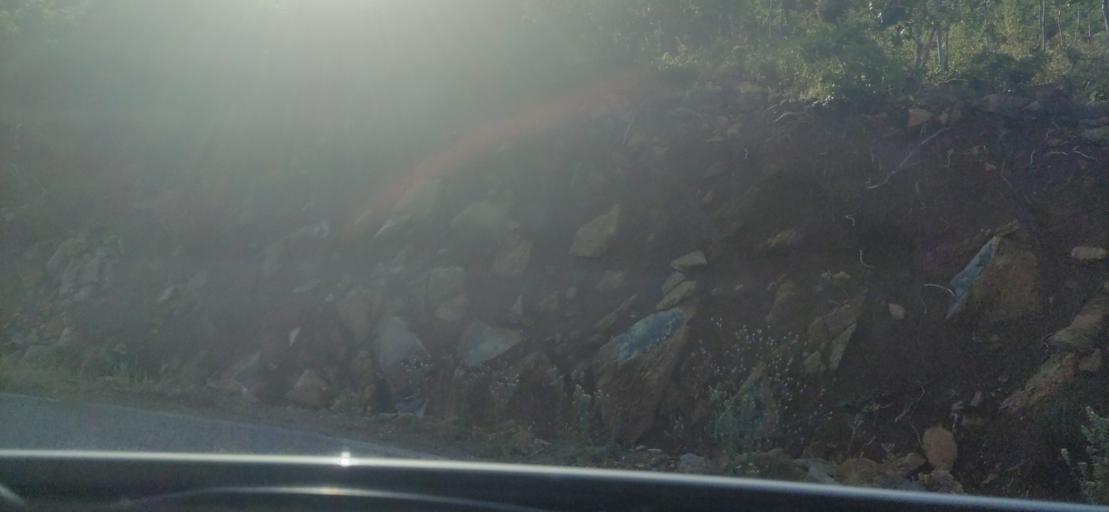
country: AL
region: Shkoder
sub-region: Rrethi i Pukes
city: Iballe
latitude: 42.1685
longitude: 20.0029
